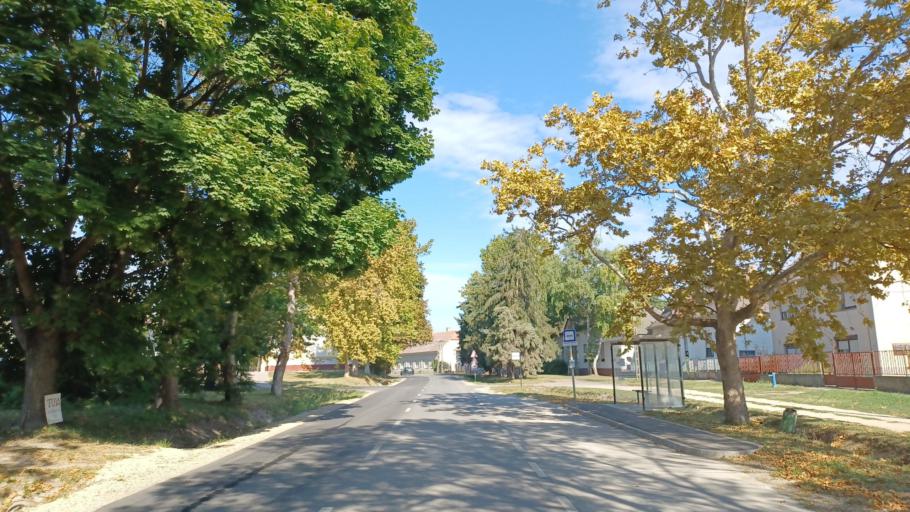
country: HU
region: Tolna
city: Dunaszentgyorgy
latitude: 46.5265
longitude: 18.8269
